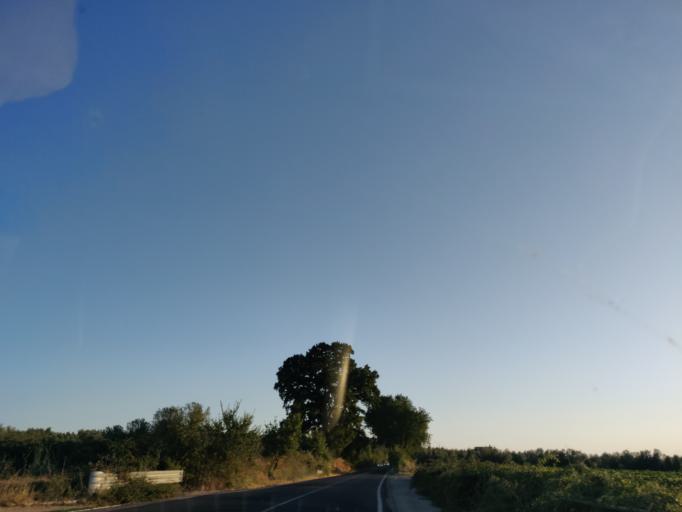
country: IT
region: Latium
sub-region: Provincia di Viterbo
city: Canino
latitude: 42.4262
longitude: 11.7108
